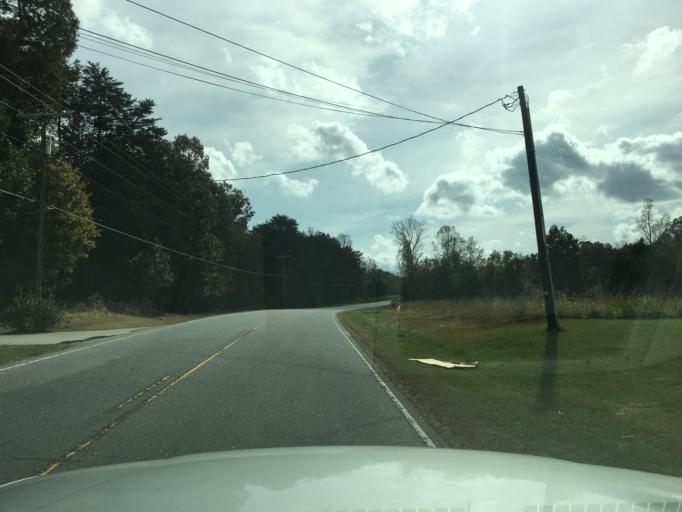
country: US
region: North Carolina
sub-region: Catawba County
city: Newton
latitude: 35.6654
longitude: -81.2722
